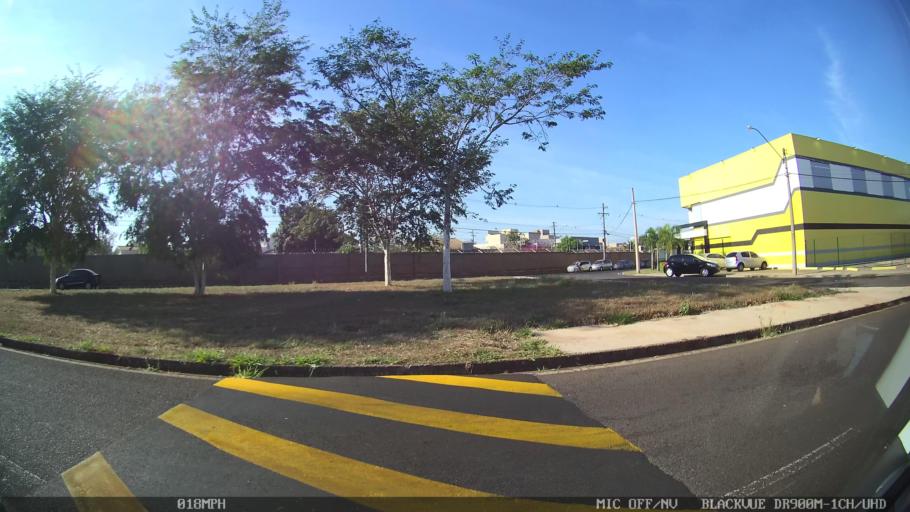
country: BR
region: Sao Paulo
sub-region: Sao Jose Do Rio Preto
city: Sao Jose do Rio Preto
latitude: -20.7786
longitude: -49.3428
